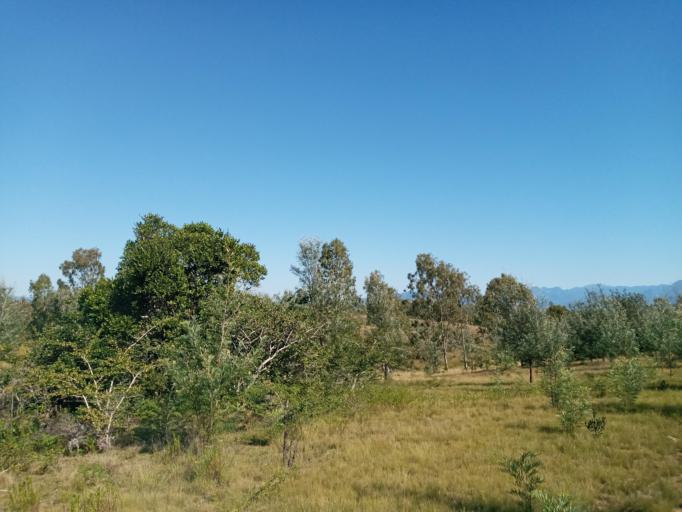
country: MG
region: Atsimo-Atsinanana
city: Vohipaho
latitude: -24.2456
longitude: 47.3152
